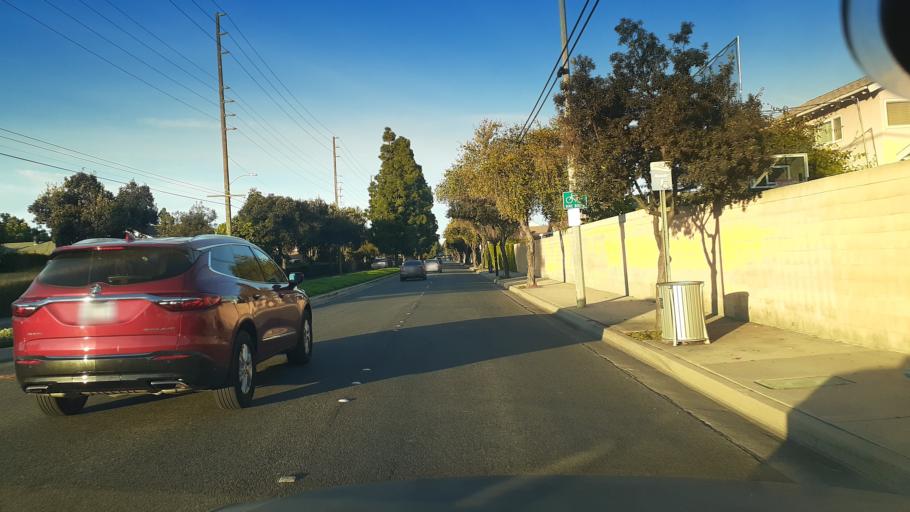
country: US
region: California
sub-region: Los Angeles County
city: Artesia
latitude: 33.8535
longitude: -118.0858
